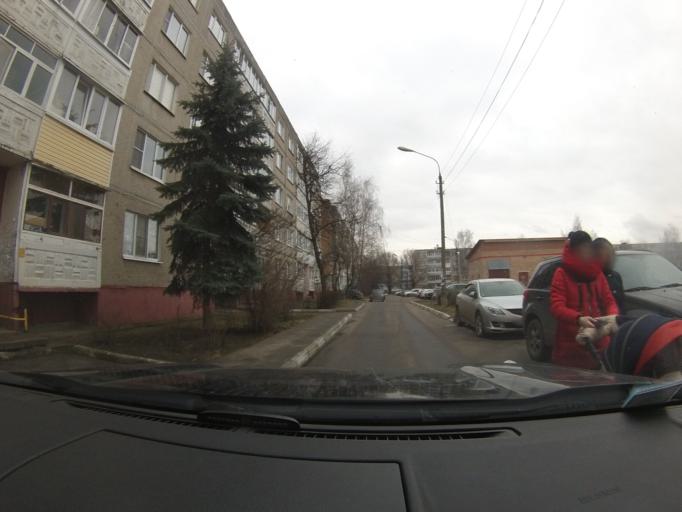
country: RU
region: Moskovskaya
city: Lopatinskiy
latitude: 55.3395
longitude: 38.7154
